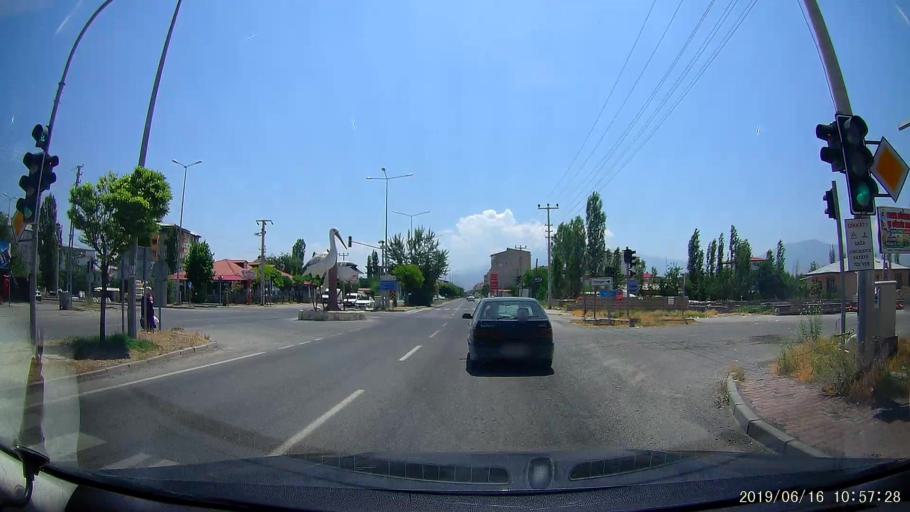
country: TR
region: Igdir
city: Igdir
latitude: 39.9276
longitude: 44.0261
